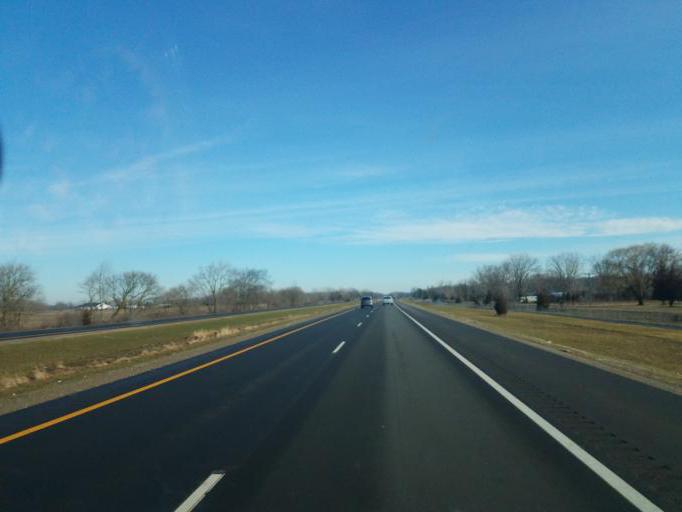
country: US
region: Michigan
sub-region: Gratiot County
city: Ithaca
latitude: 43.3441
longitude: -84.6015
